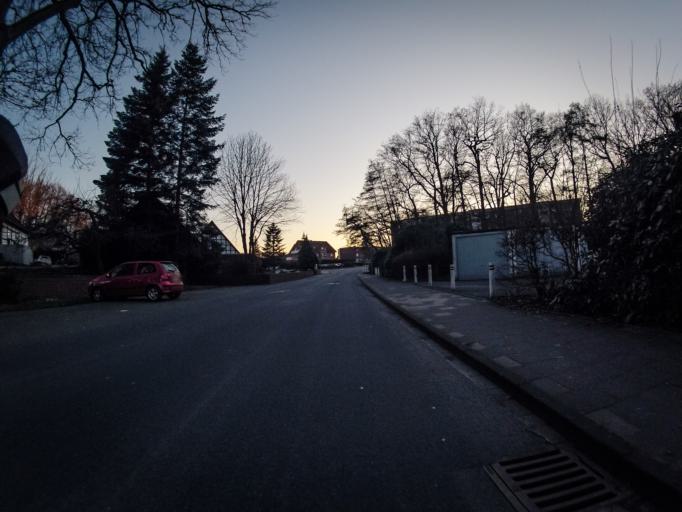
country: DE
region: North Rhine-Westphalia
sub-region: Regierungsbezirk Munster
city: Lotte
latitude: 52.3097
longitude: 7.9427
